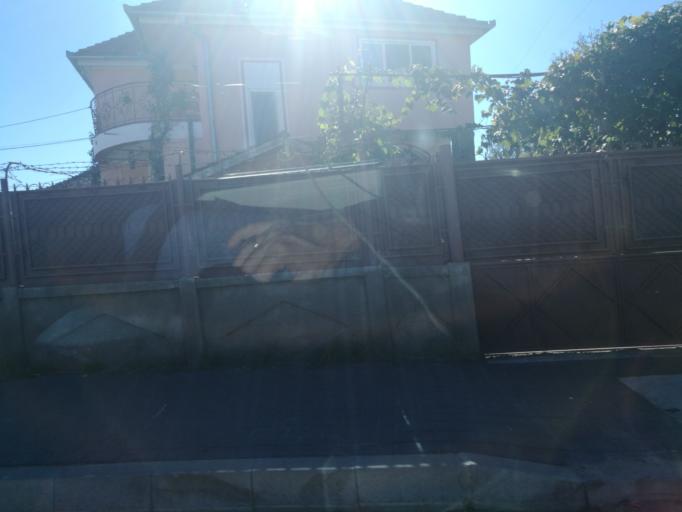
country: RO
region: Brasov
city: Fogarasch
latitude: 45.8406
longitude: 24.9735
